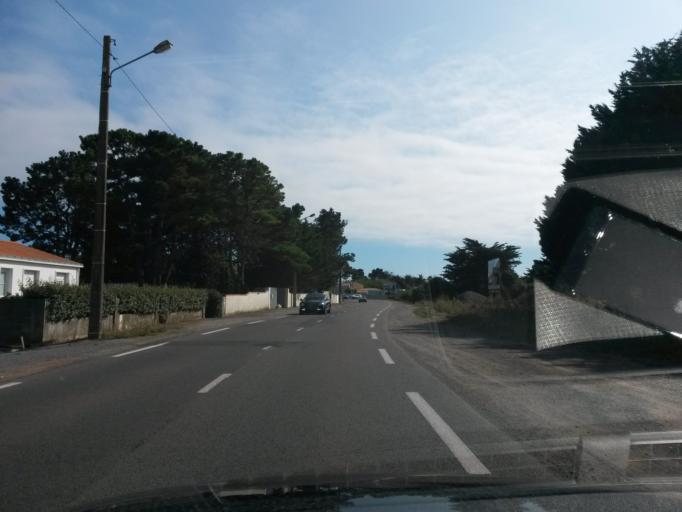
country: FR
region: Pays de la Loire
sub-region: Departement de la Vendee
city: Olonne-sur-Mer
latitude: 46.5512
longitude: -1.8065
